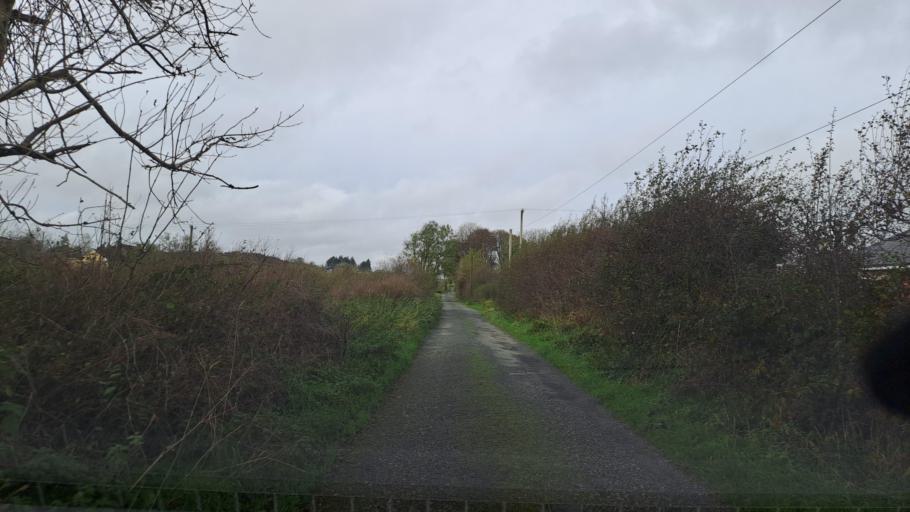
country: IE
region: Ulster
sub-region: County Monaghan
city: Carrickmacross
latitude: 54.0122
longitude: -6.8021
